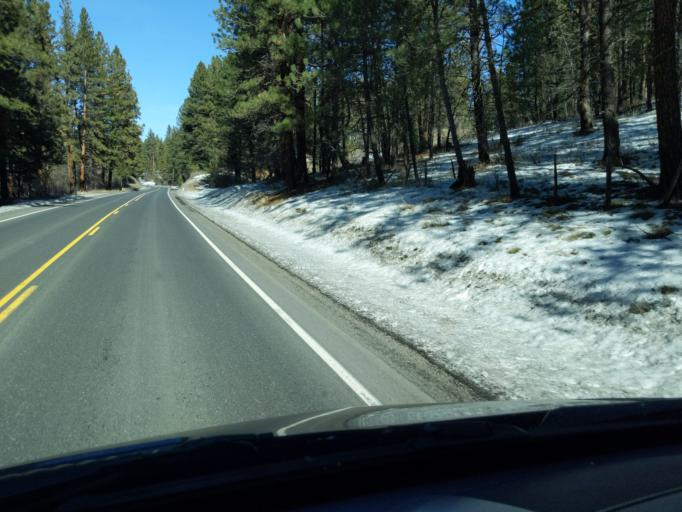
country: US
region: Oregon
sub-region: Grant County
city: John Day
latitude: 44.8736
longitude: -119.0195
